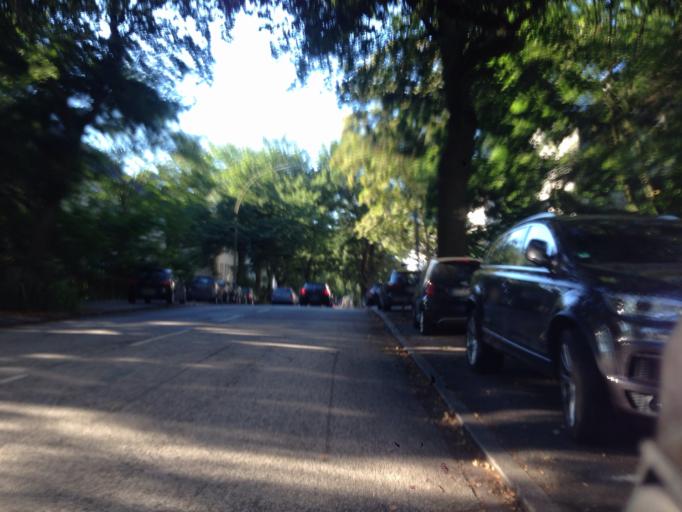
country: DE
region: Hamburg
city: Hamburg
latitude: 53.5831
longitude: 10.0059
